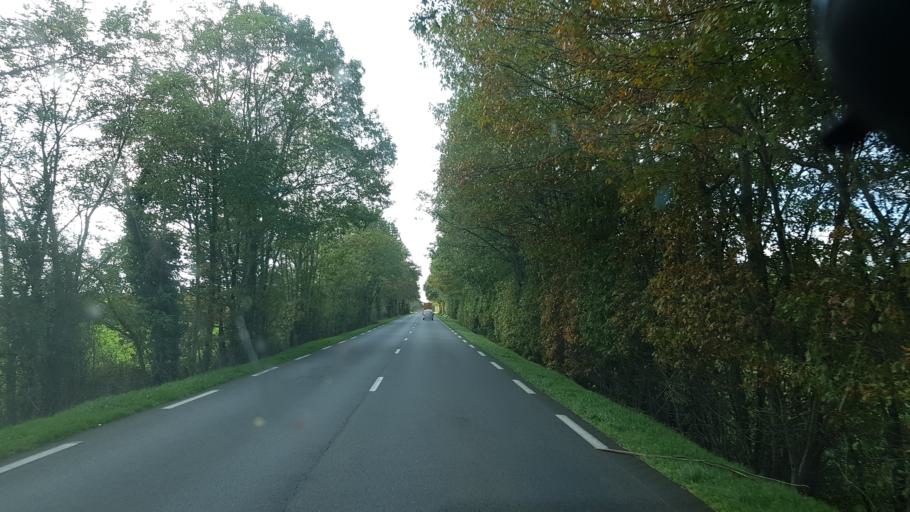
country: FR
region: Poitou-Charentes
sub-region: Departement de la Charente
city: Confolens
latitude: 46.0682
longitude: 0.7194
